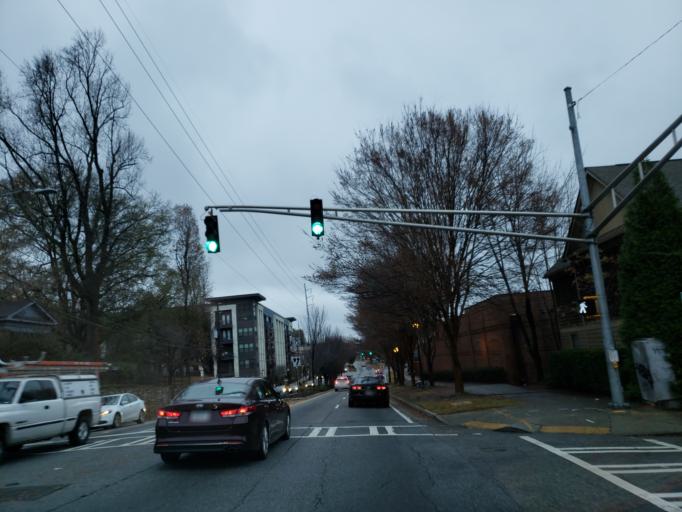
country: US
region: Georgia
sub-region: DeKalb County
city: Druid Hills
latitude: 33.7553
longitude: -84.3492
